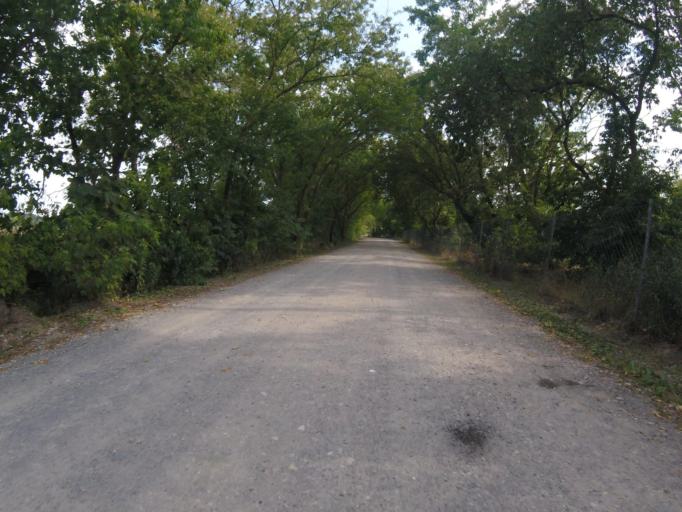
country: DE
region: Brandenburg
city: Spreenhagen
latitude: 52.3021
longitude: 13.7811
